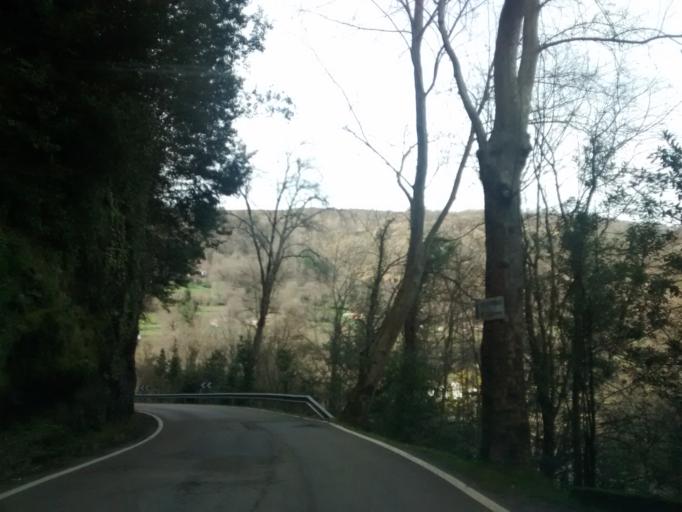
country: ES
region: Cantabria
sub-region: Provincia de Cantabria
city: Selaya
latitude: 43.1720
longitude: -3.8688
